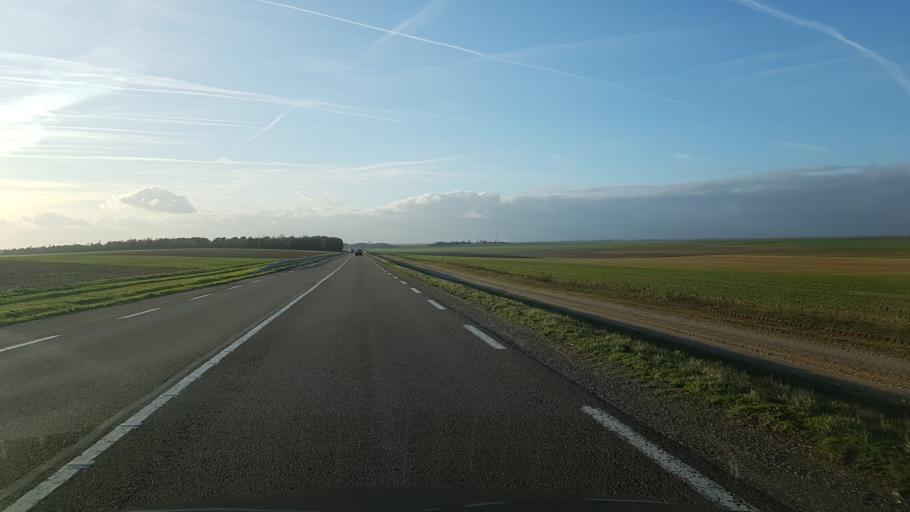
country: FR
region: Champagne-Ardenne
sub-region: Departement de l'Aube
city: Mailly-le-Camp
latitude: 48.7337
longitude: 4.2777
